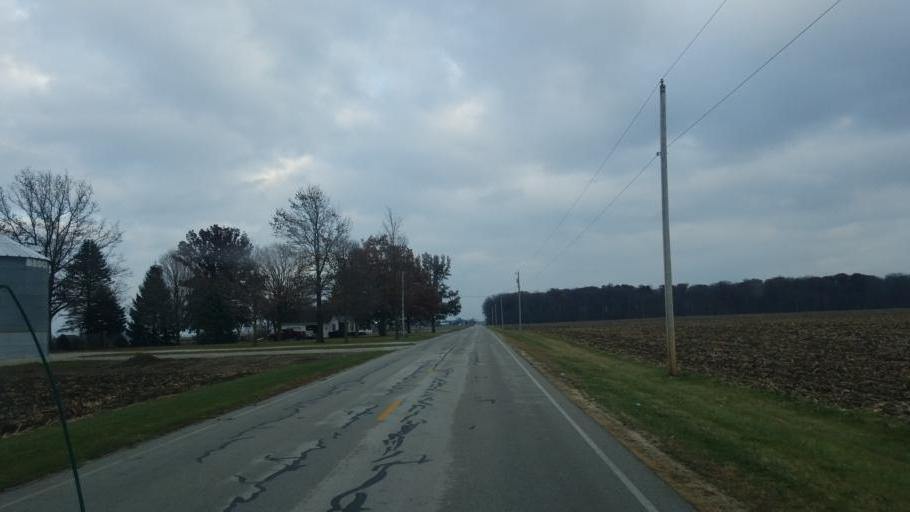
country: US
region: Ohio
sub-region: Mercer County
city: Coldwater
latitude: 40.5089
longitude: -84.6452
